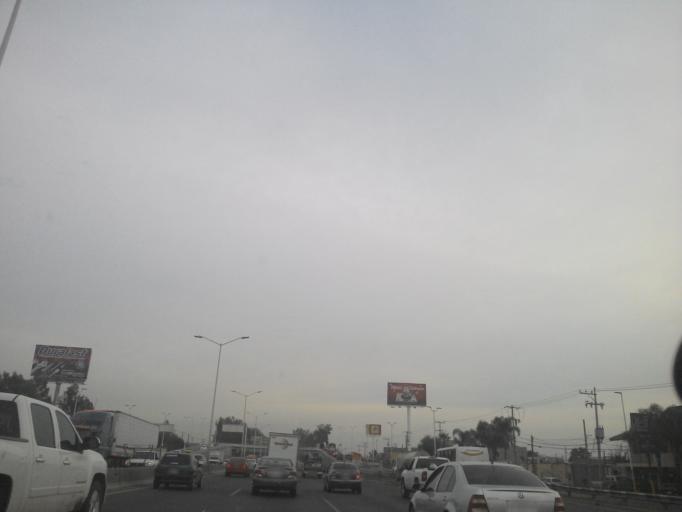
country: MX
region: Jalisco
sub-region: San Pedro Tlaquepaque
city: Paseo del Prado
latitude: 20.6029
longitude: -103.3974
